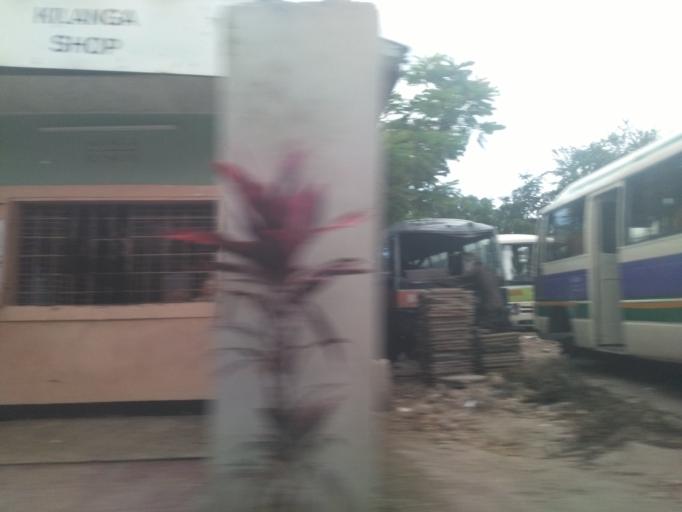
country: TZ
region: Dar es Salaam
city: Magomeni
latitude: -6.7945
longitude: 39.2735
